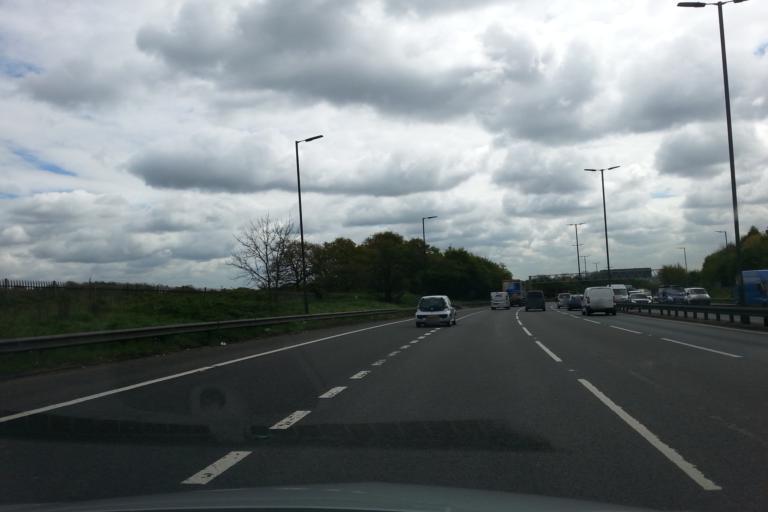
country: GB
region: England
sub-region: Walsall
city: Streetly
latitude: 52.5524
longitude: -1.9264
